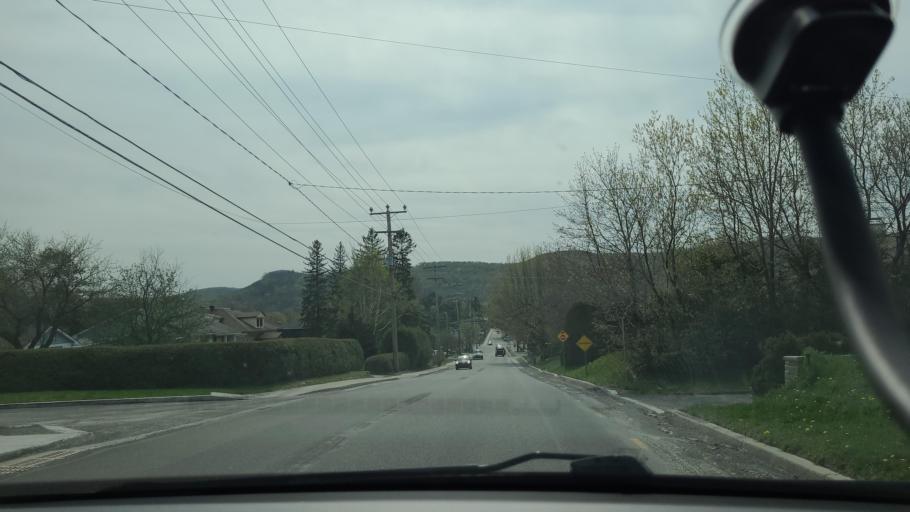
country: CA
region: Quebec
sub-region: Laurentides
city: Prevost
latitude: 45.8741
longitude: -74.0740
